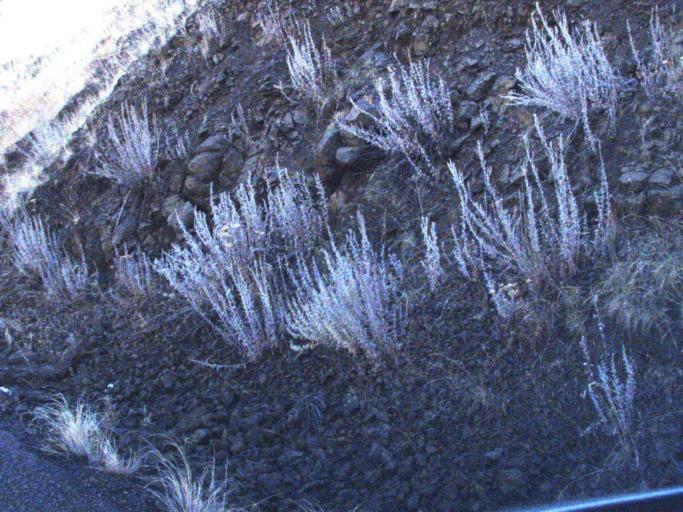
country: US
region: Washington
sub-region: Asotin County
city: Asotin
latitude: 46.0498
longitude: -117.2330
